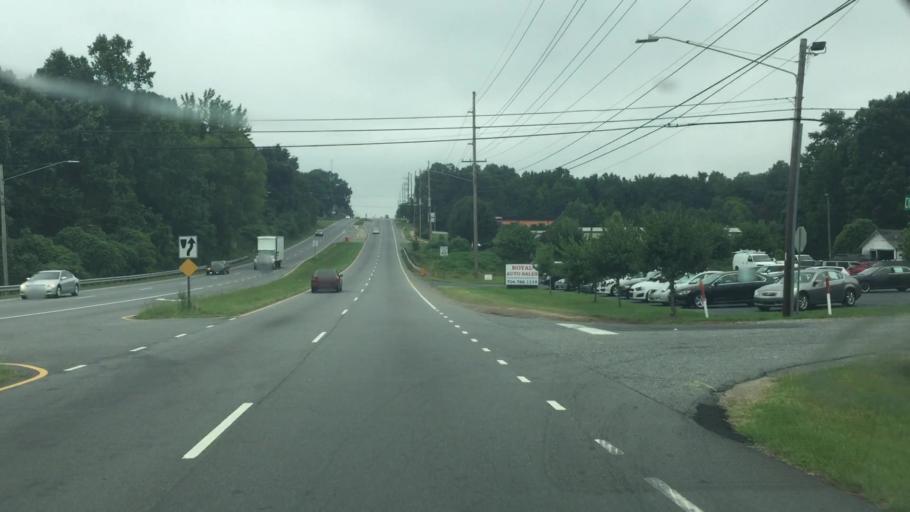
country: US
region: North Carolina
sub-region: Cabarrus County
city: Concord
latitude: 35.4080
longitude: -80.6110
